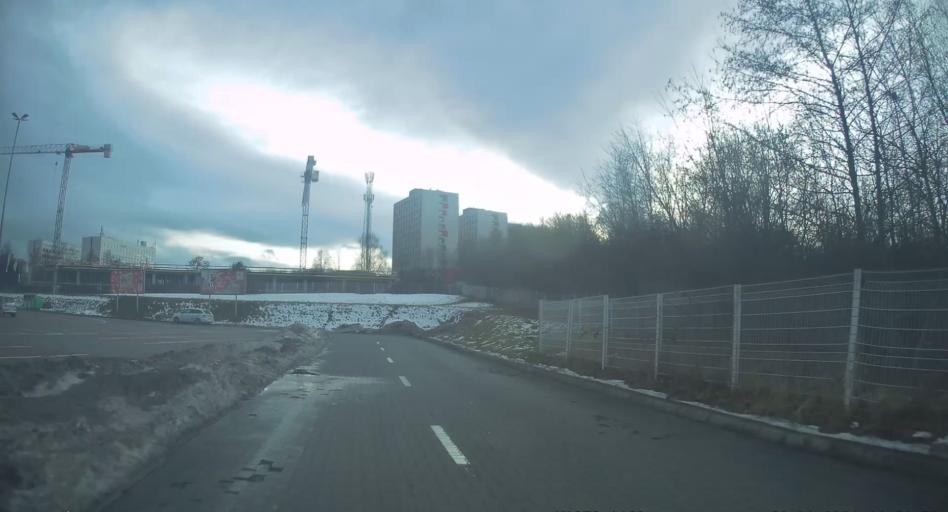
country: PL
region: Lesser Poland Voivodeship
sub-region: Powiat krakowski
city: Ochojno
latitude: 50.0147
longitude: 19.9930
